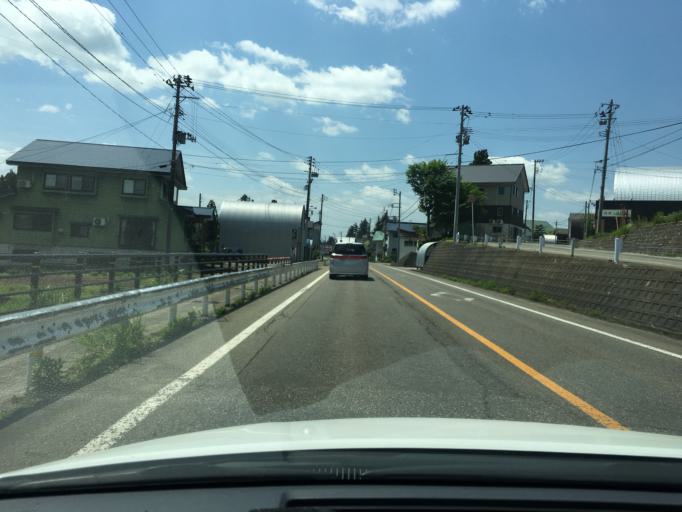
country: JP
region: Niigata
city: Tochio-honcho
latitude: 37.2937
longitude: 138.9909
